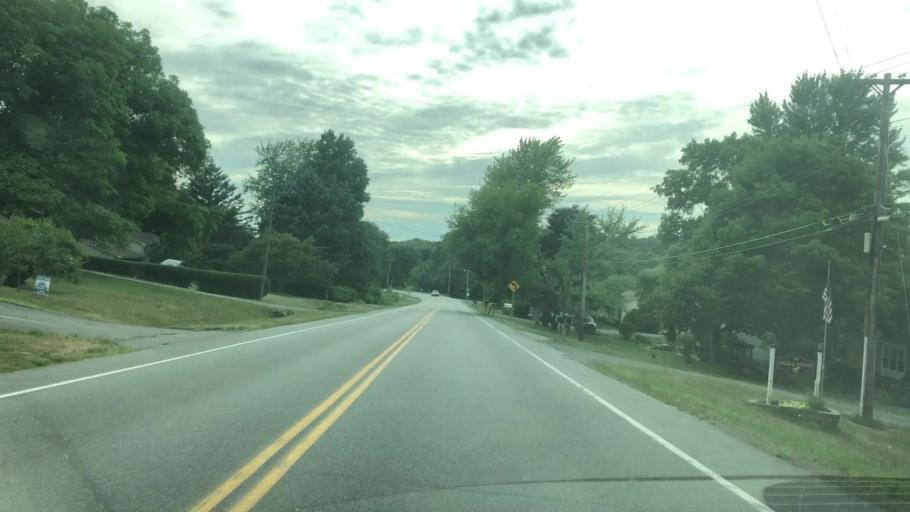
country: US
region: New York
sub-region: Monroe County
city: Fairport
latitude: 43.1349
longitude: -77.3606
